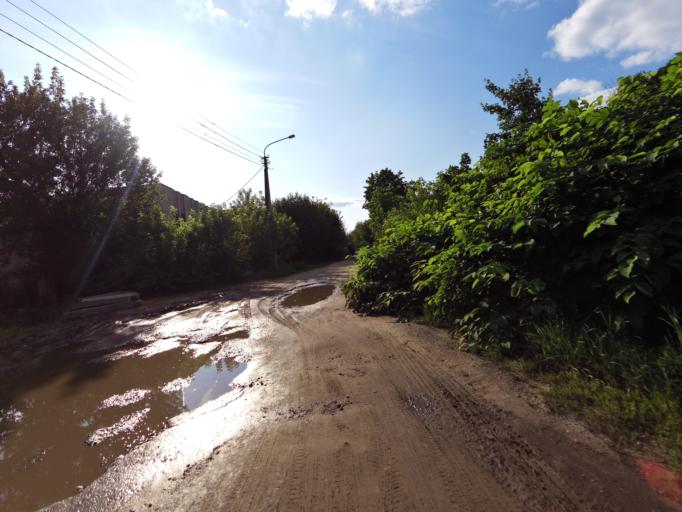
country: LT
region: Vilnius County
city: Rasos
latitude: 54.6792
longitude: 25.3077
